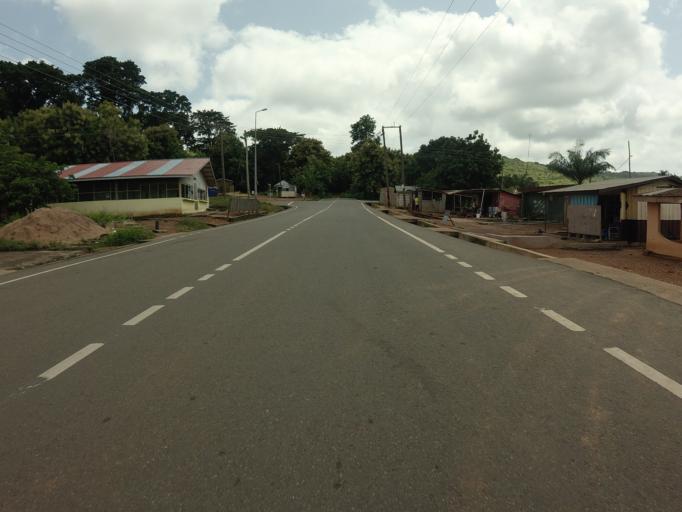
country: GH
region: Volta
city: Ho
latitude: 6.6130
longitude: 0.4593
